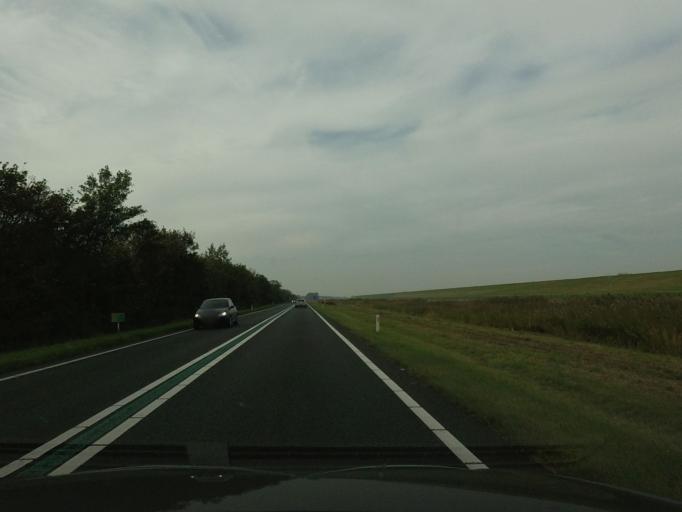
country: NL
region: North Holland
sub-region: Gemeente Den Helder
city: Den Helder
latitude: 52.9039
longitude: 4.8241
